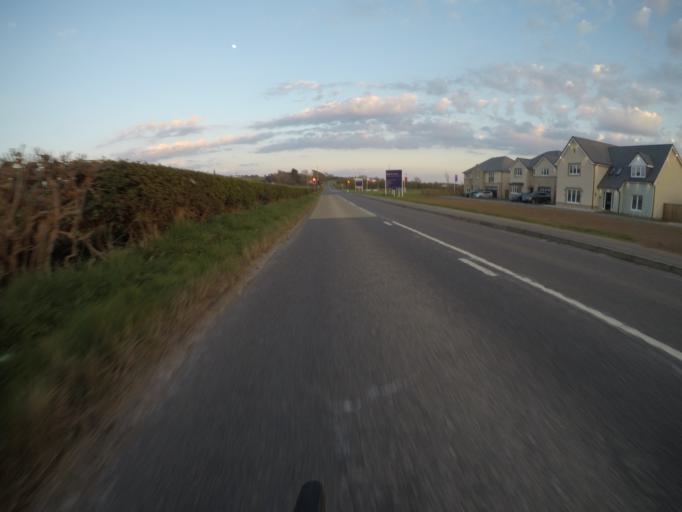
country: GB
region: Scotland
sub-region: South Ayrshire
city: Troon
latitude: 55.5585
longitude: -4.6291
